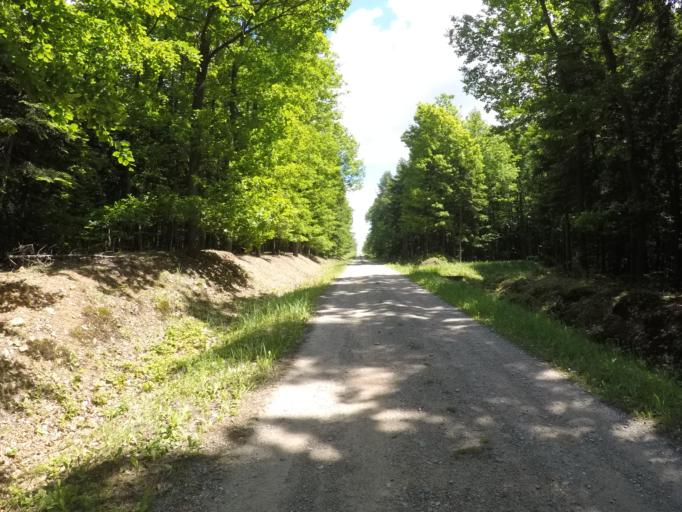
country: PL
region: Swietokrzyskie
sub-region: Powiat kielecki
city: Kostomloty Pierwsze
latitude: 50.9345
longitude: 20.6152
